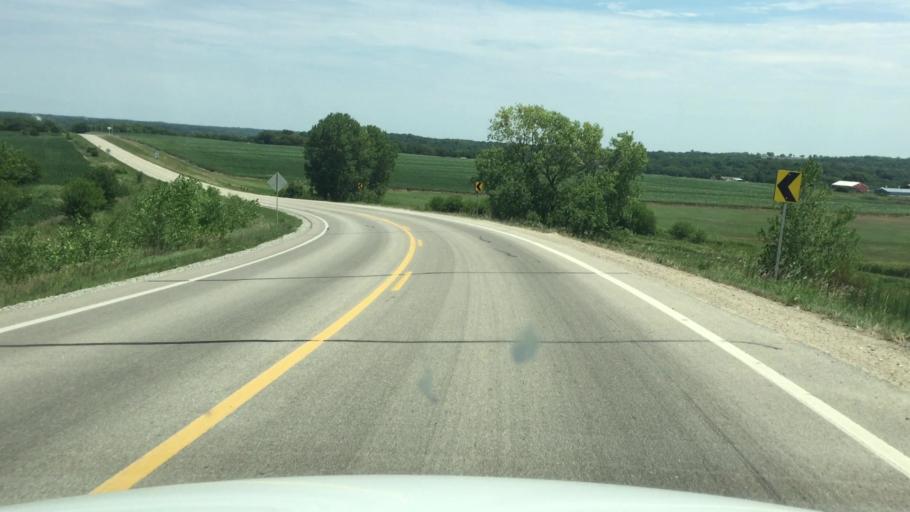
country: US
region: Kansas
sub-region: Osage County
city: Overbrook
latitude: 38.9715
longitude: -95.4900
